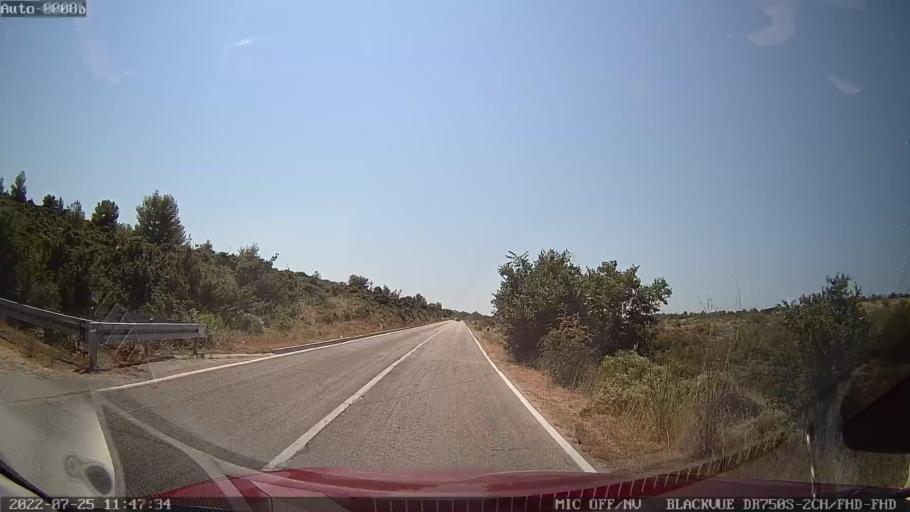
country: HR
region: Zadarska
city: Razanac
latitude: 44.2373
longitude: 15.3022
